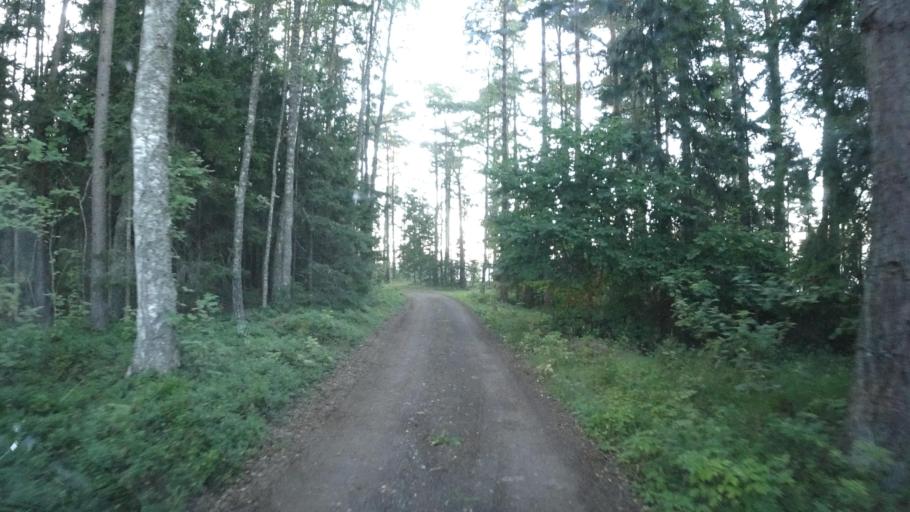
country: LV
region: Rojas
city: Roja
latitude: 57.4844
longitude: 22.8530
